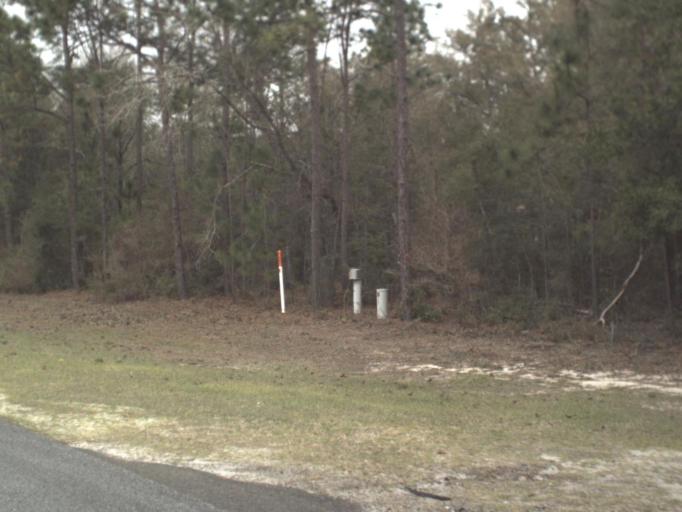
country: US
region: Florida
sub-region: Wakulla County
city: Crawfordville
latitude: 30.1419
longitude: -84.3095
